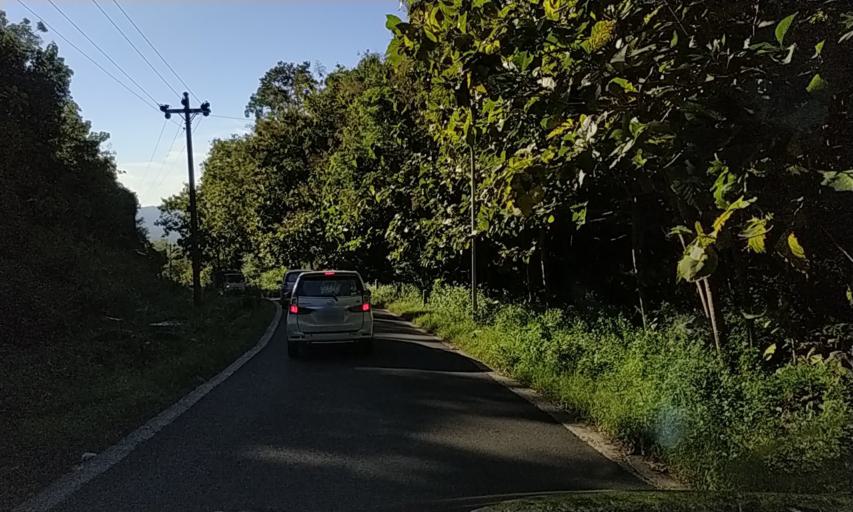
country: ID
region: East Java
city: Krajan
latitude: -8.0899
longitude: 110.8740
